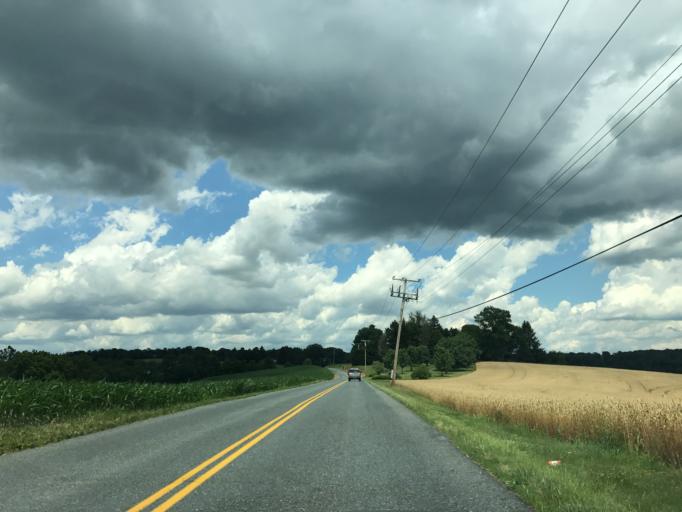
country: US
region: Maryland
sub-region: Harford County
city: Jarrettsville
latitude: 39.6653
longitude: -76.4458
